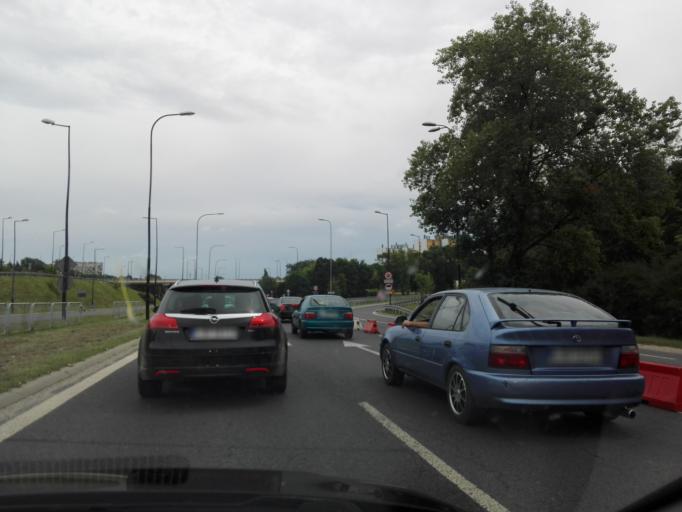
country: PL
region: Lublin Voivodeship
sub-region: Powiat lubelski
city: Lublin
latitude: 51.2561
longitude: 22.5401
